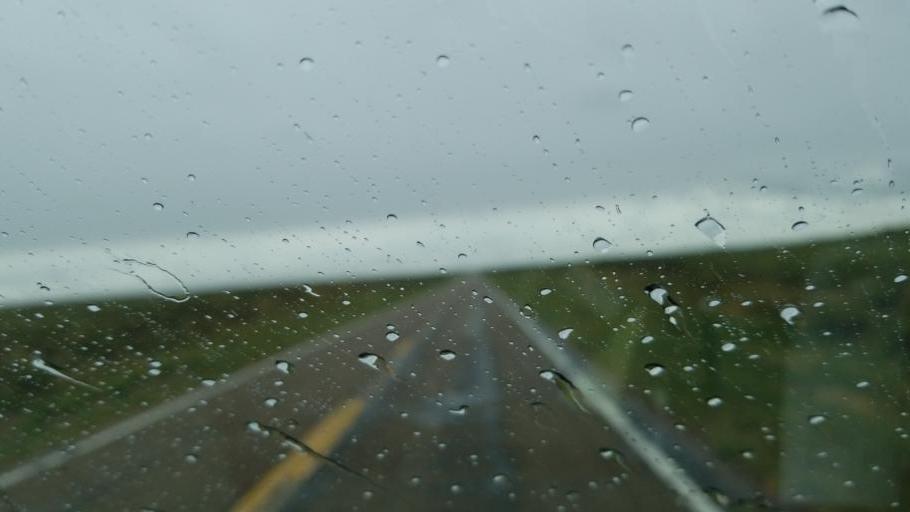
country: US
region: Colorado
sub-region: Lincoln County
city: Hugo
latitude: 38.8495
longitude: -103.2221
